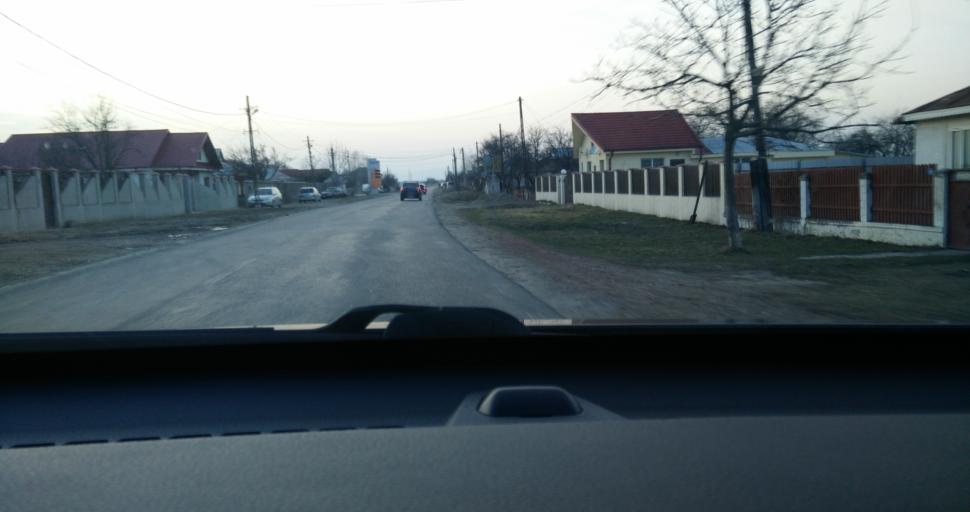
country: RO
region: Vrancea
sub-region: Comuna Rastoaca
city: Rastoaca
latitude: 45.6663
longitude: 27.2690
